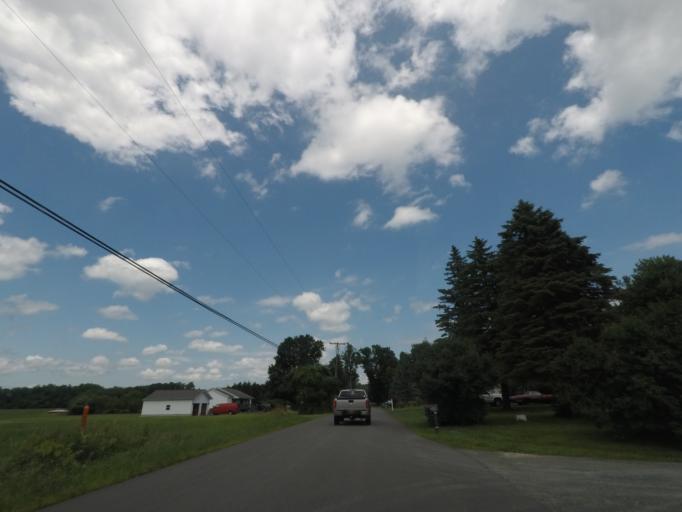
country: US
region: New York
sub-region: Rensselaer County
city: East Greenbush
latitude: 42.5314
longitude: -73.6902
